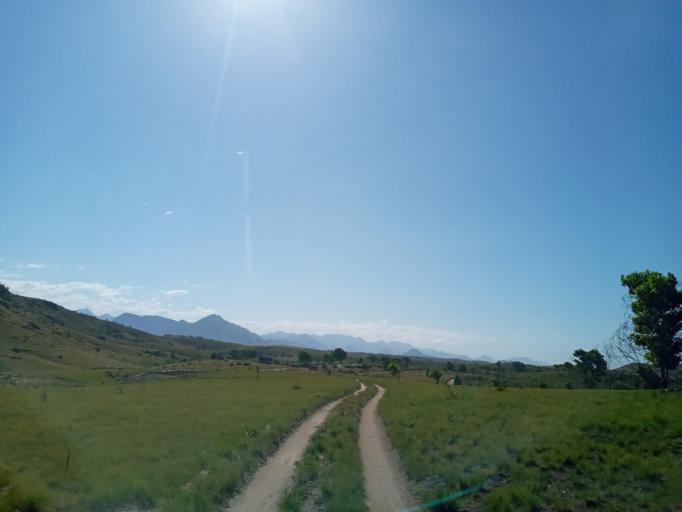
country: MG
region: Anosy
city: Fort Dauphin
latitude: -24.9100
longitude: 47.0906
